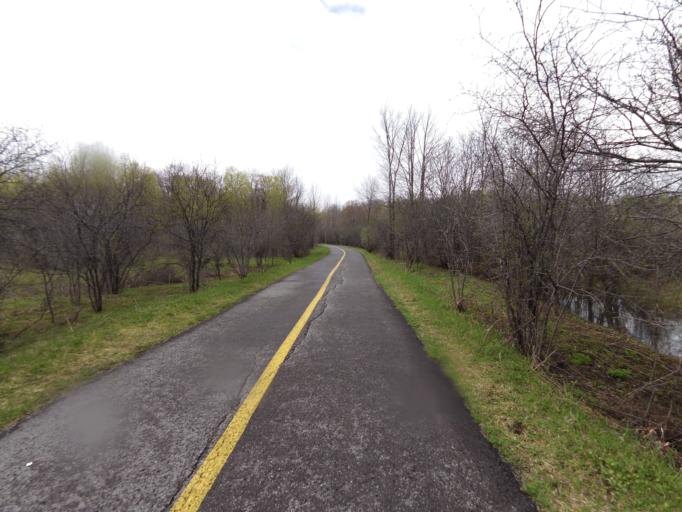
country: CA
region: Quebec
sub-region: Outaouais
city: Gatineau
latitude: 45.4660
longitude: -75.7874
